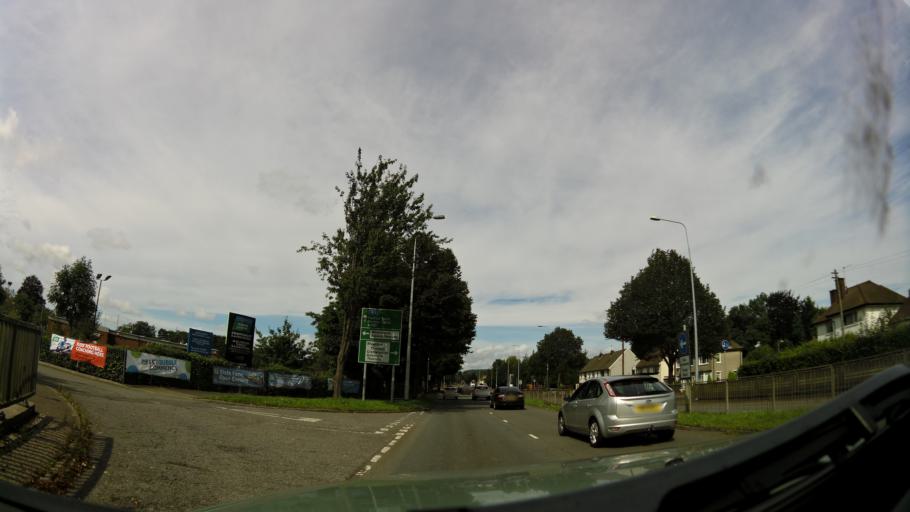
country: GB
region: Wales
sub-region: Cardiff
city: Radyr
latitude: 51.5159
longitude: -3.2147
